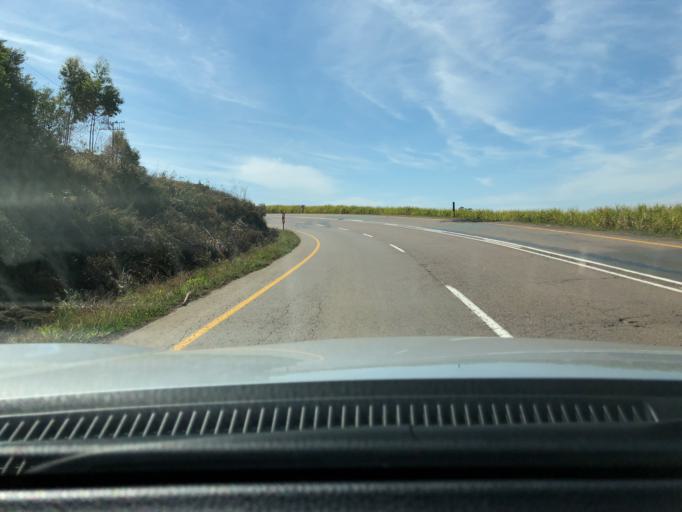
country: ZA
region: KwaZulu-Natal
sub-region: uMgungundlovu District Municipality
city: Richmond
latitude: -29.8172
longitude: 30.3433
